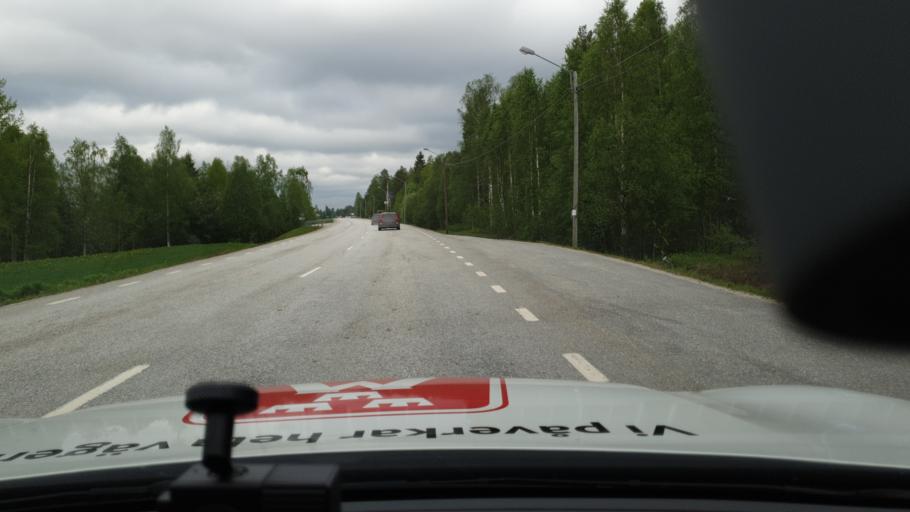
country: SE
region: Vaesterbotten
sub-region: Vannas Kommun
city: Vannasby
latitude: 64.1170
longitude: 19.9697
